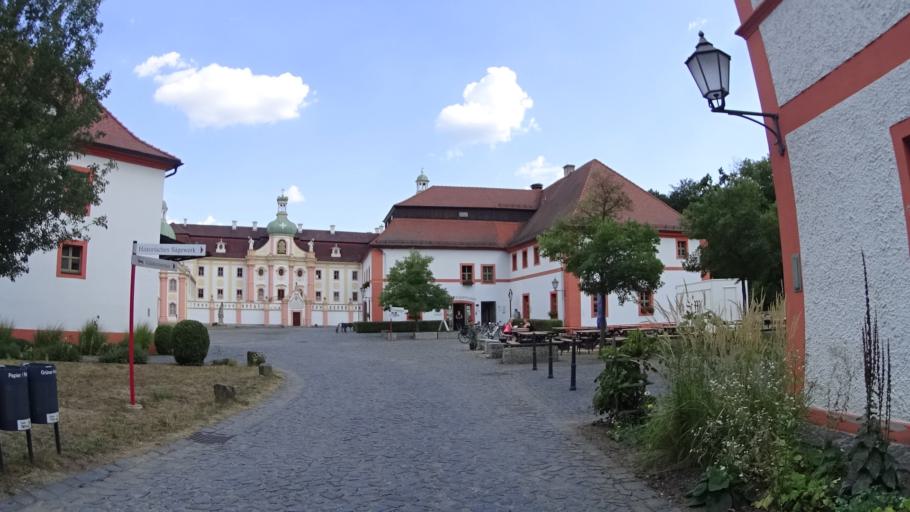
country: DE
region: Saxony
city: Ostritz
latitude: 50.9977
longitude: 14.9239
